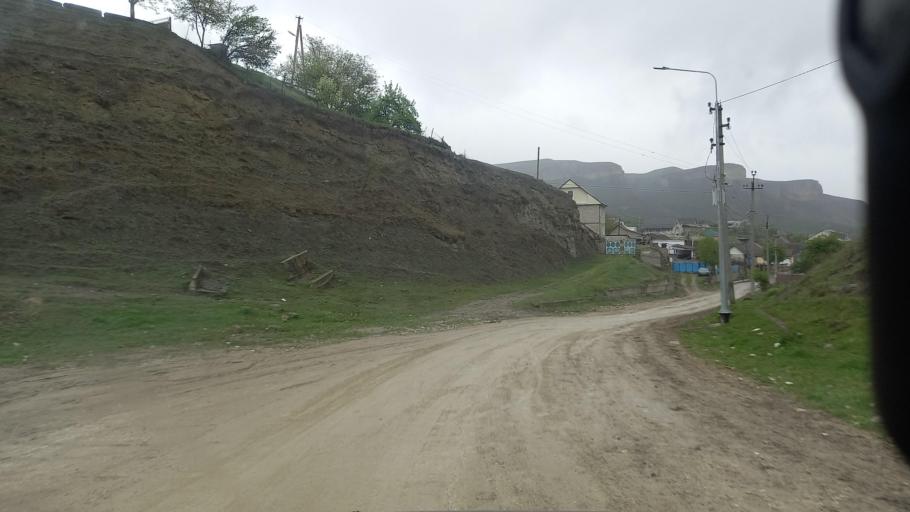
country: RU
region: Kabardino-Balkariya
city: Gundelen
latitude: 43.5996
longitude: 43.1457
